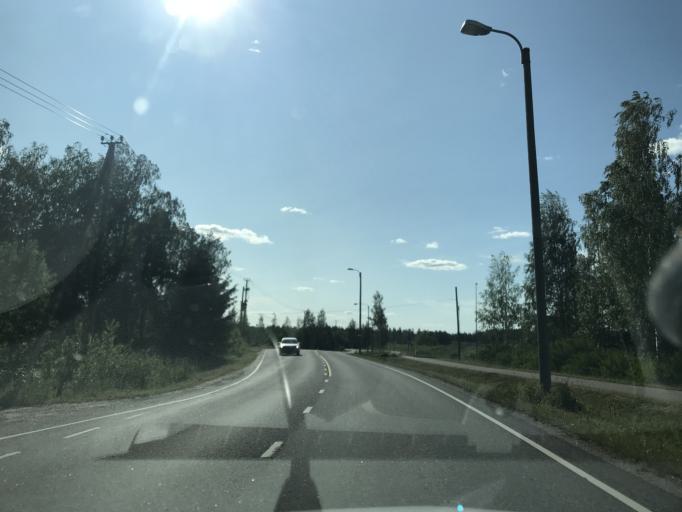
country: FI
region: Uusimaa
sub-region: Helsinki
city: Nurmijaervi
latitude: 60.3848
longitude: 24.7236
